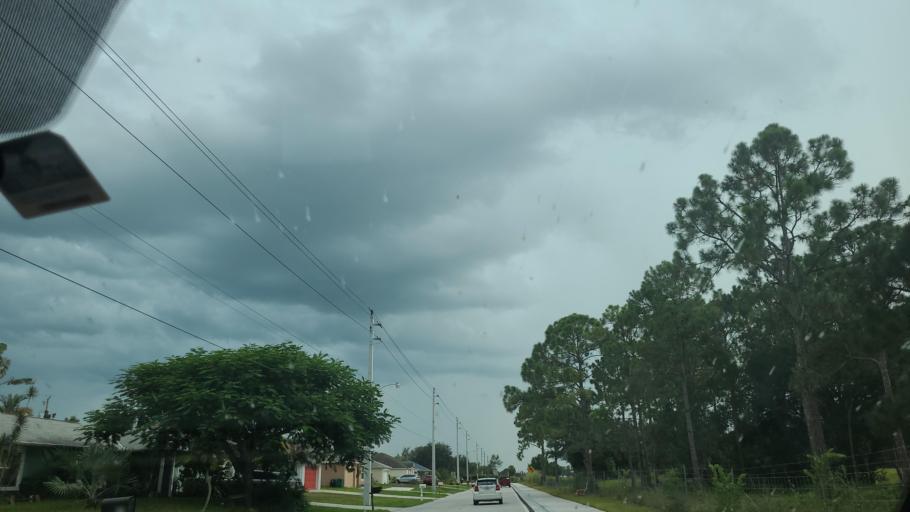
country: US
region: Florida
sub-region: Saint Lucie County
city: Port Saint Lucie
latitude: 27.2236
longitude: -80.3997
